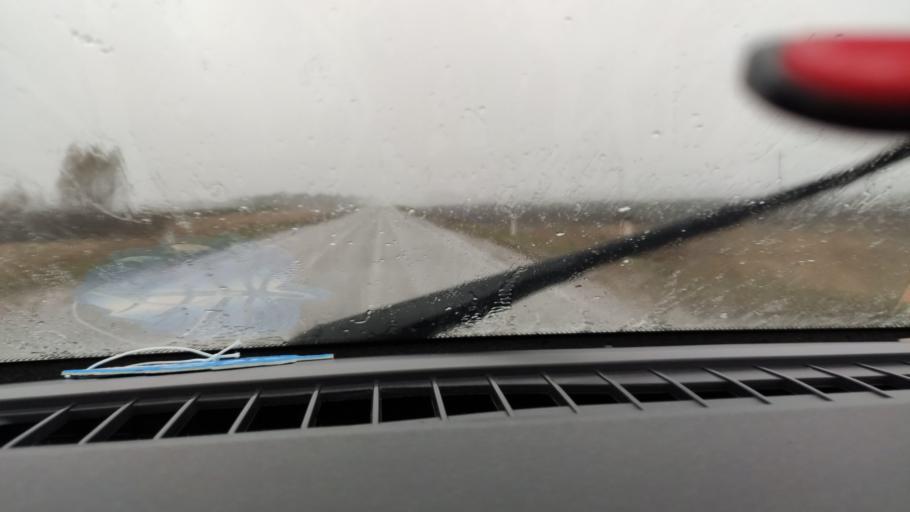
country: RU
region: Tatarstan
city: Cheremshan
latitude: 54.7243
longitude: 51.3011
